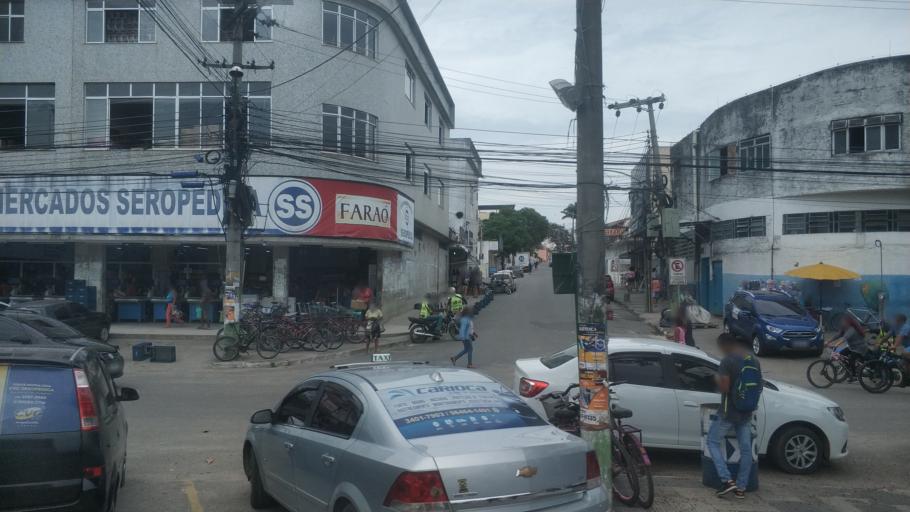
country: BR
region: Rio de Janeiro
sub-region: Seropedica
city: Seropedica
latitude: -22.7452
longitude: -43.7016
